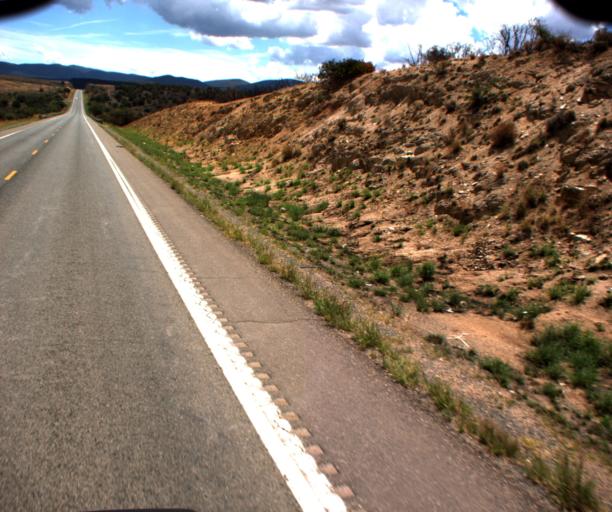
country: US
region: Arizona
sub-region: Yavapai County
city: Camp Verde
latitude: 34.5211
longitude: -112.0384
